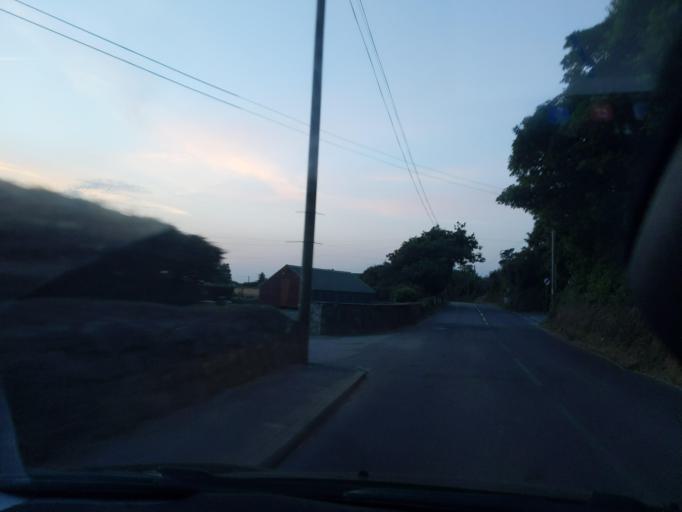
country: GB
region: England
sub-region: Cornwall
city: Camborne
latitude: 50.1787
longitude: -5.3117
